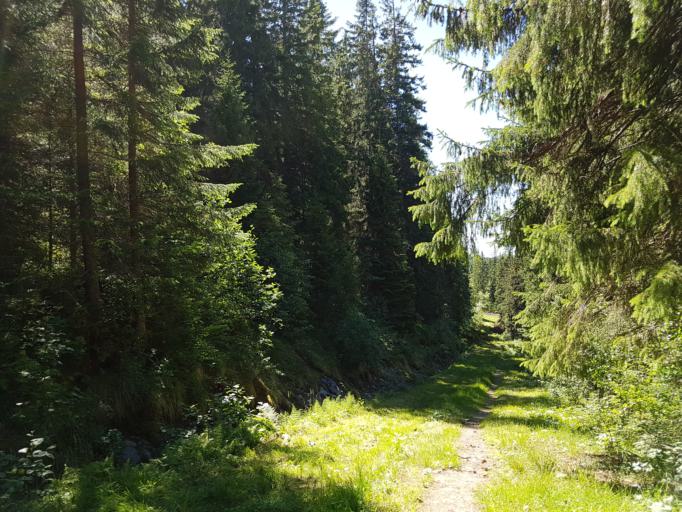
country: NO
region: Sor-Trondelag
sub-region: Melhus
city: Melhus
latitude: 63.4367
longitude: 10.2010
